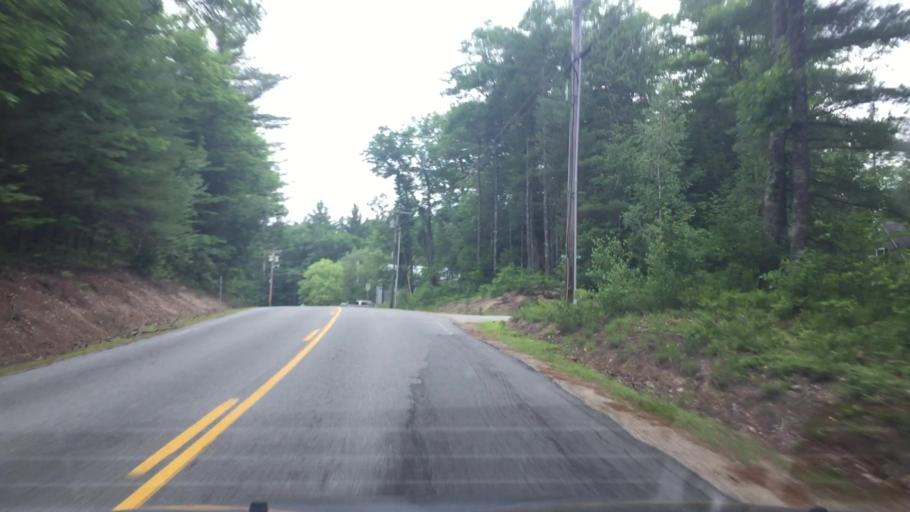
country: US
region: New Hampshire
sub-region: Carroll County
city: North Conway
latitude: 44.0788
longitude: -71.1638
